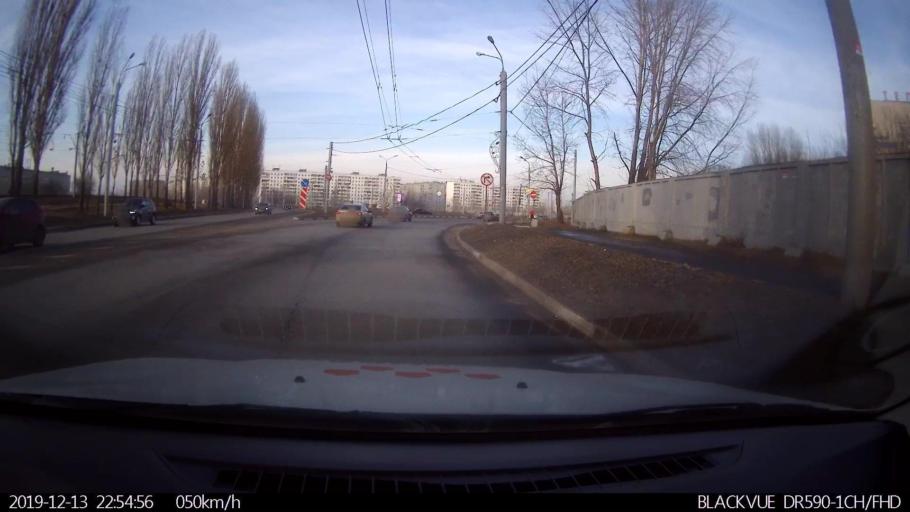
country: RU
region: Nizjnij Novgorod
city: Nizhniy Novgorod
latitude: 56.3284
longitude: 43.9495
